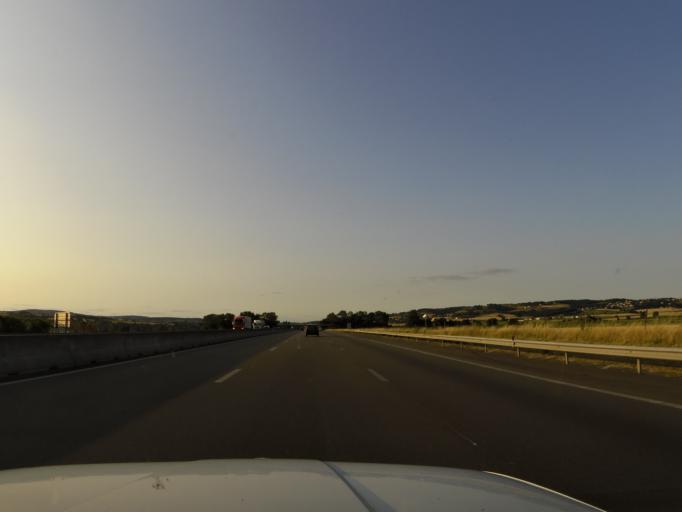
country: FR
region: Rhone-Alpes
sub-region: Departement de l'Isere
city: Auberives-sur-Vareze
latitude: 45.4417
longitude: 4.8264
